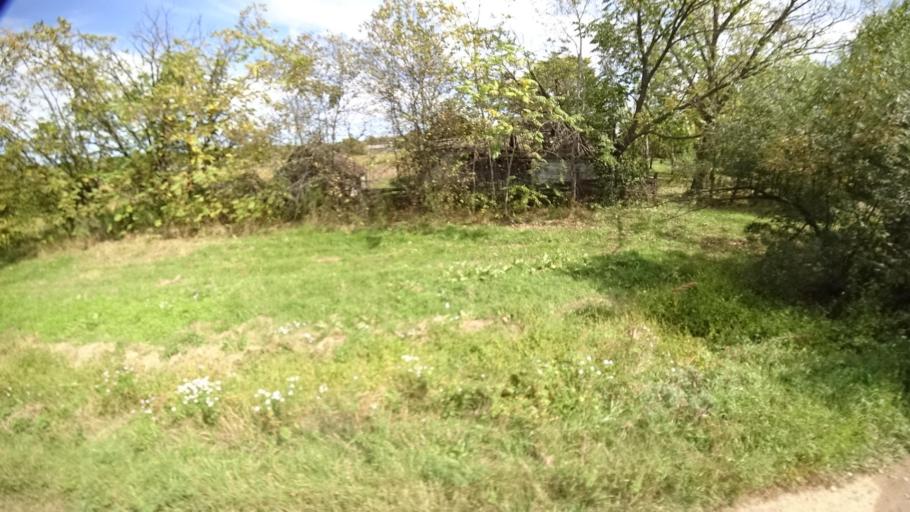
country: RU
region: Primorskiy
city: Yakovlevka
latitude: 44.6462
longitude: 133.5883
